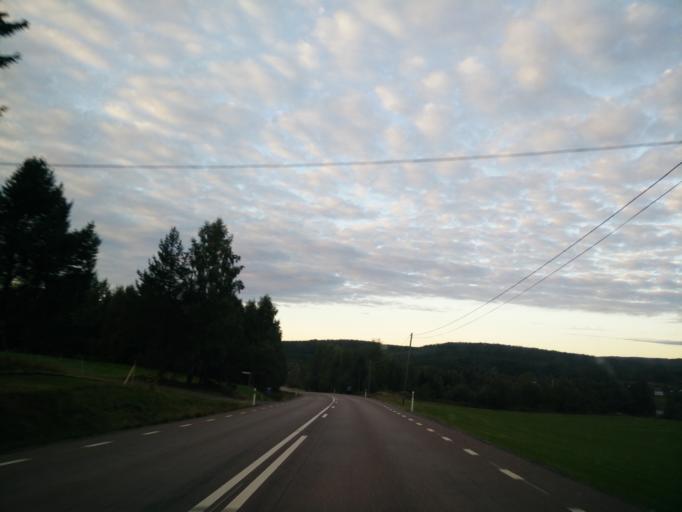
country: SE
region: Vaesternorrland
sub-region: Kramfors Kommun
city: Nordingra
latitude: 62.9244
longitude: 18.0792
